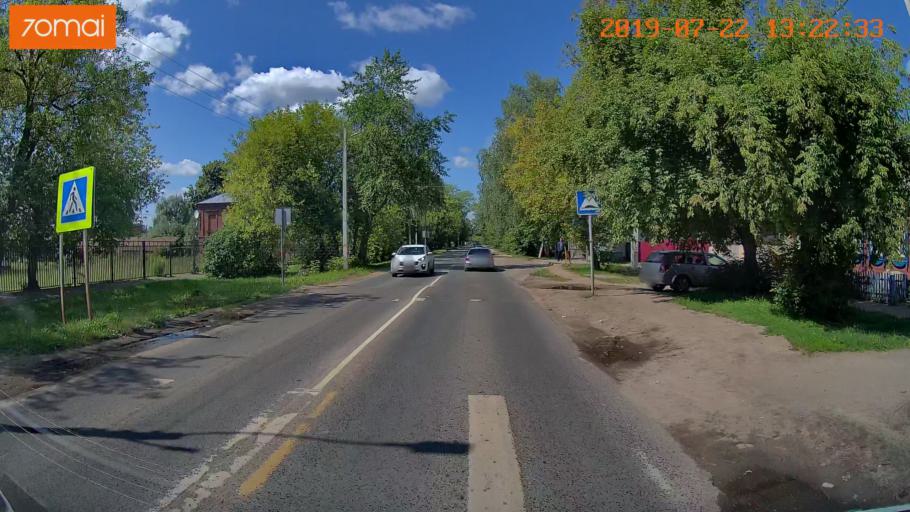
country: RU
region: Ivanovo
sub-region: Gorod Ivanovo
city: Ivanovo
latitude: 57.0241
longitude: 40.9559
